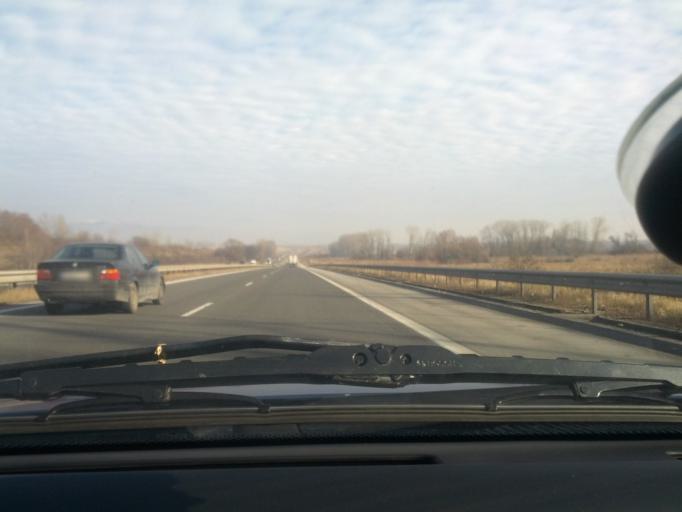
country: BG
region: Sofia-Capital
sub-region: Stolichna Obshtina
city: Bukhovo
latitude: 42.7160
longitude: 23.4860
